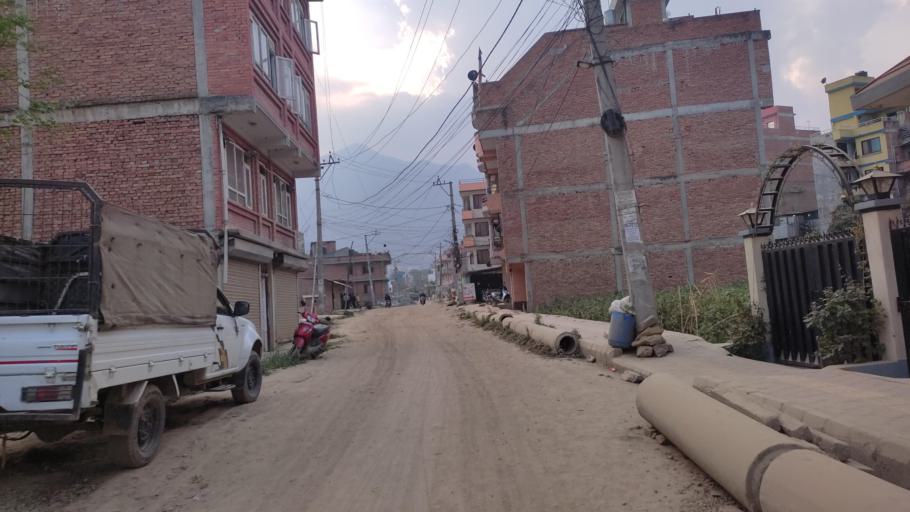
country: NP
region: Central Region
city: Kirtipur
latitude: 27.6677
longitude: 85.2763
